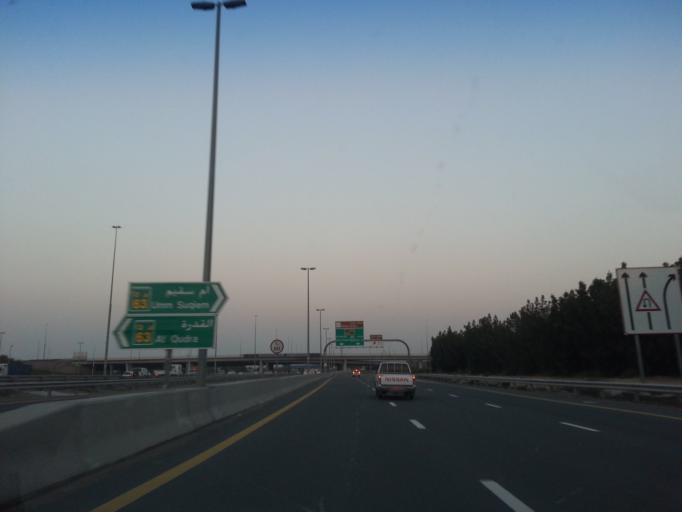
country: AE
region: Dubai
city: Dubai
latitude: 25.0549
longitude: 55.2430
